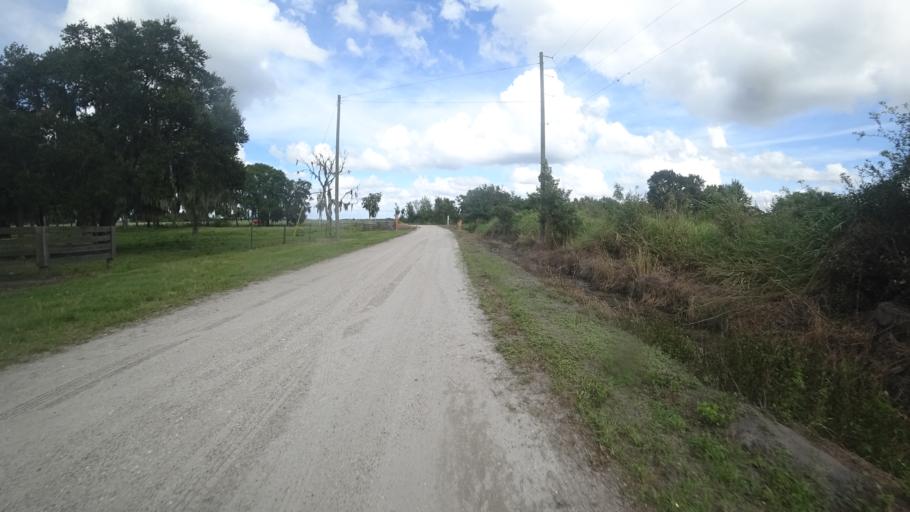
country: US
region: Florida
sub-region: Hillsborough County
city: Wimauma
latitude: 27.5945
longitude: -82.2720
